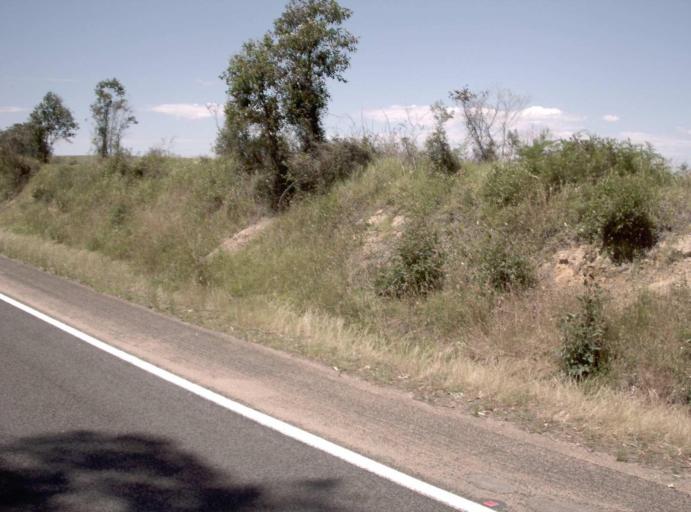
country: AU
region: Victoria
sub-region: East Gippsland
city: Lakes Entrance
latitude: -37.7041
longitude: 148.5149
